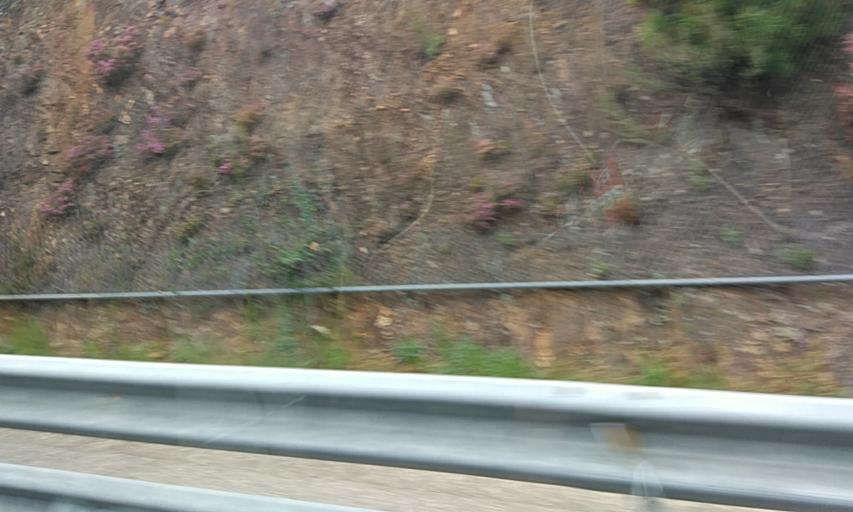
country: ES
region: Extremadura
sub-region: Provincia de Caceres
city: Perales del Puerto
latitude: 40.1672
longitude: -6.6801
